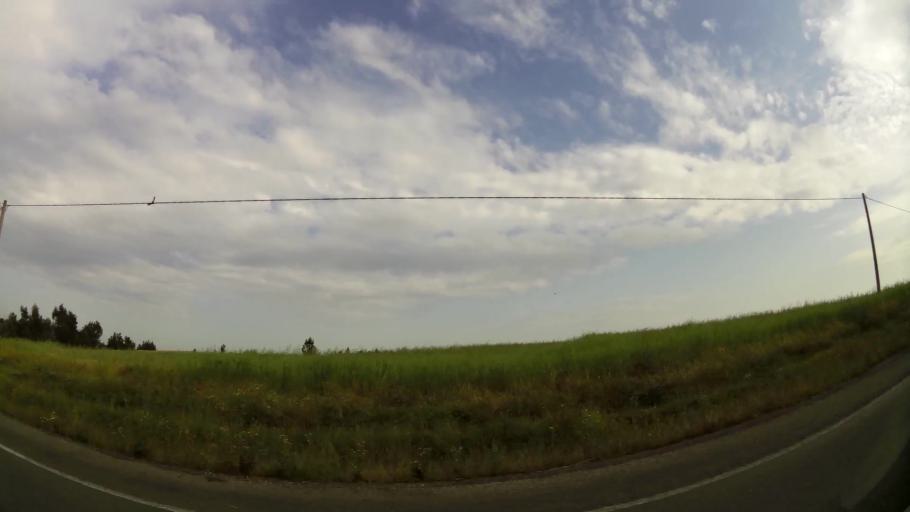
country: MA
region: Rabat-Sale-Zemmour-Zaer
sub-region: Khemisset
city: Khemisset
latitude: 33.7942
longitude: -6.1036
